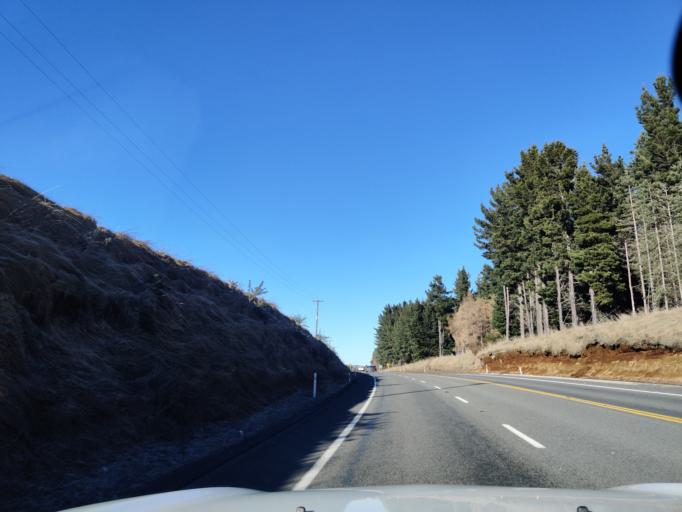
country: NZ
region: Manawatu-Wanganui
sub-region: Ruapehu District
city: Waiouru
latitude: -39.4493
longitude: 175.6786
